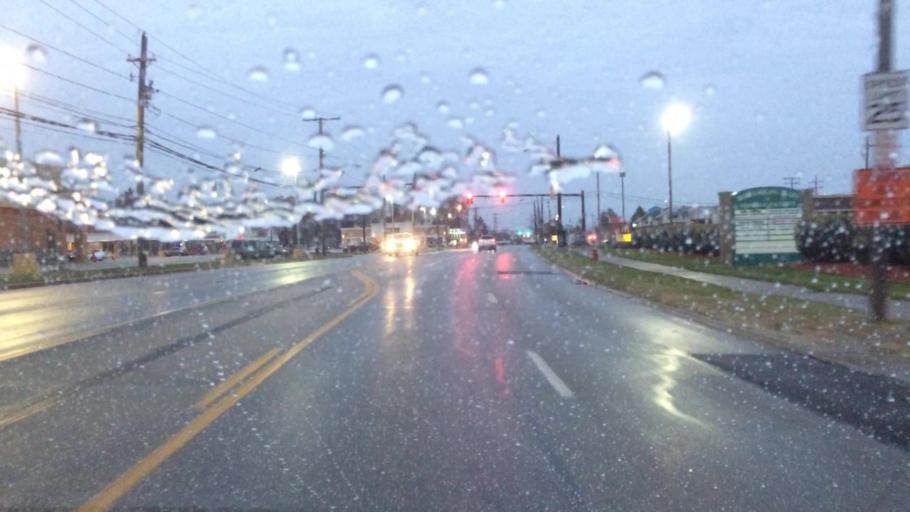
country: US
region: Ohio
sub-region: Cuyahoga County
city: Berea
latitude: 41.3725
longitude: -81.8657
